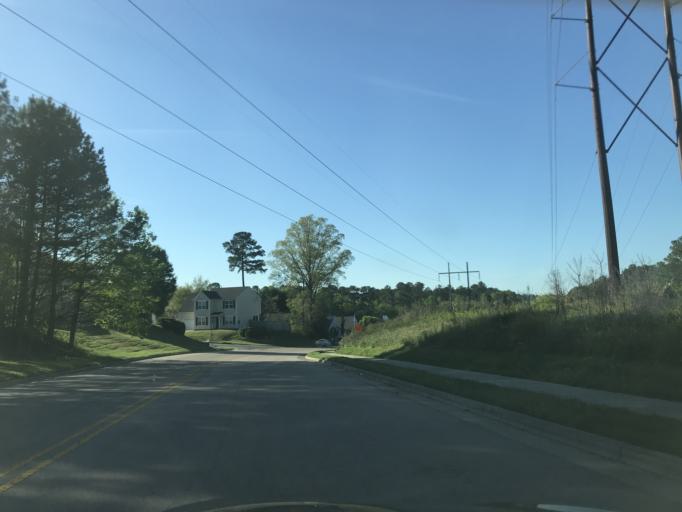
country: US
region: North Carolina
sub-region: Wake County
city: Raleigh
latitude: 35.8413
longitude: -78.5666
